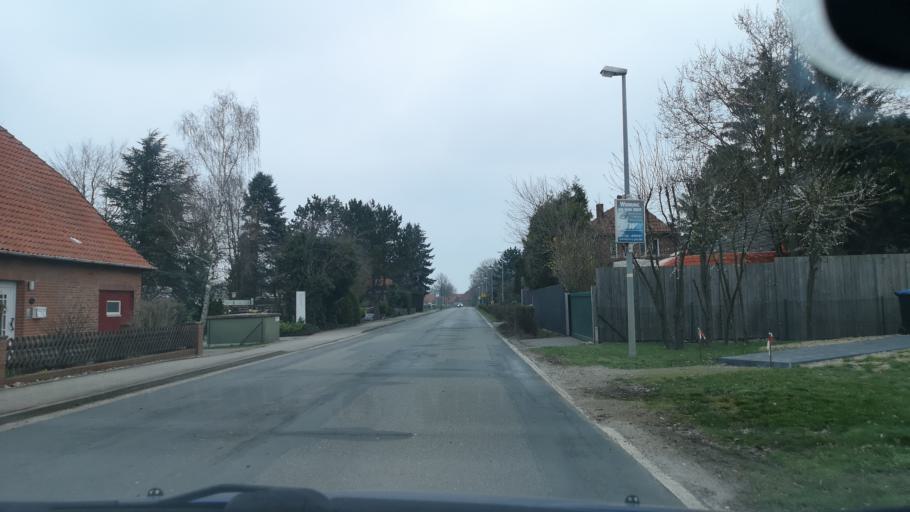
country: DE
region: Lower Saxony
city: Schwarmstedt
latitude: 52.5970
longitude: 9.5626
